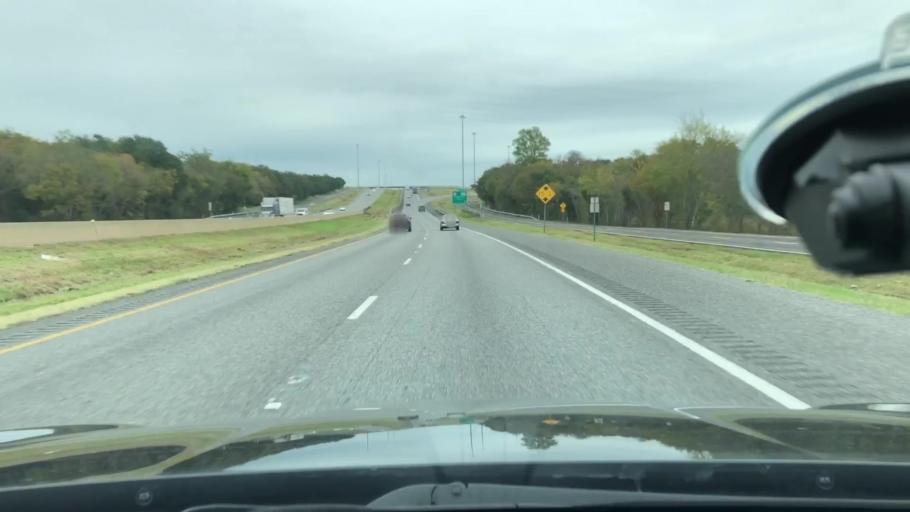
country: US
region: Texas
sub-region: Hunt County
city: Greenville
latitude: 33.1298
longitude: -96.0018
